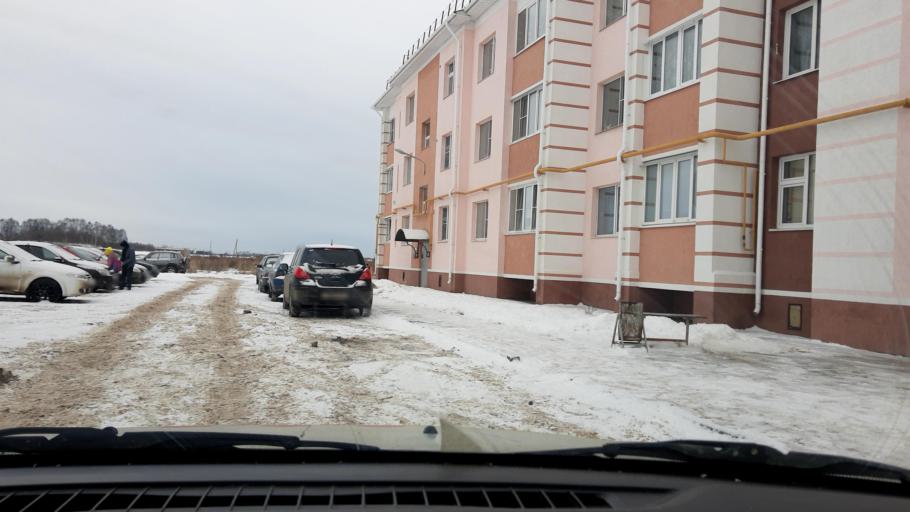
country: RU
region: Nizjnij Novgorod
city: Gorodets
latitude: 56.6684
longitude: 43.4770
